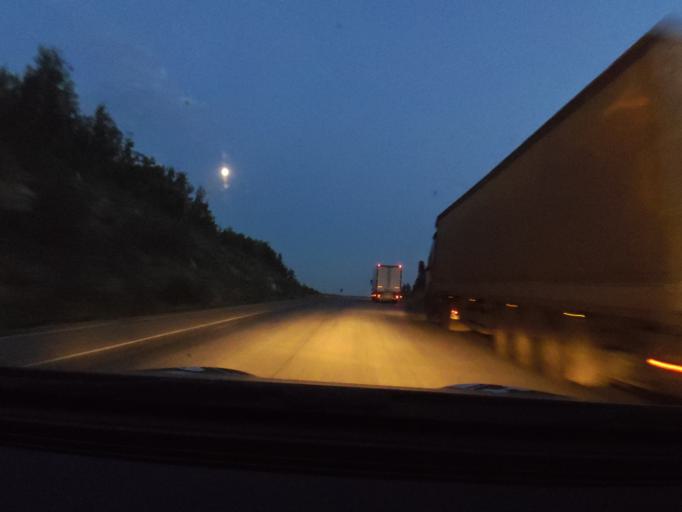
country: RU
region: Bashkortostan
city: Duvan
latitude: 55.9597
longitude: 58.2001
